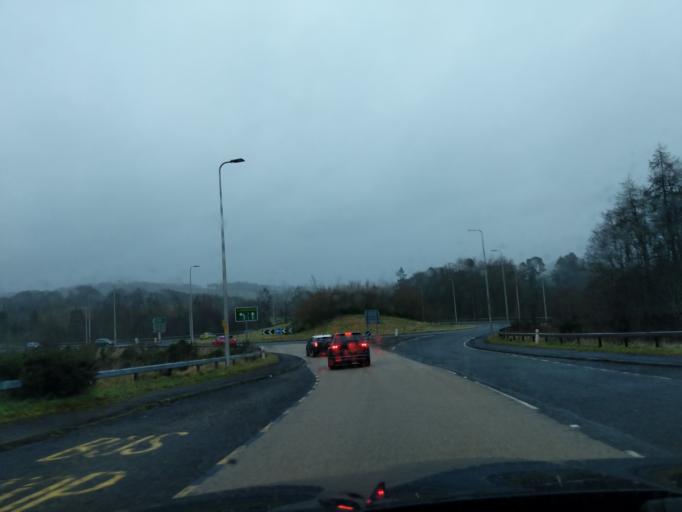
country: GB
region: Scotland
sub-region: The Scottish Borders
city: Newtown St Boswells
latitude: 55.5950
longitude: -2.6708
